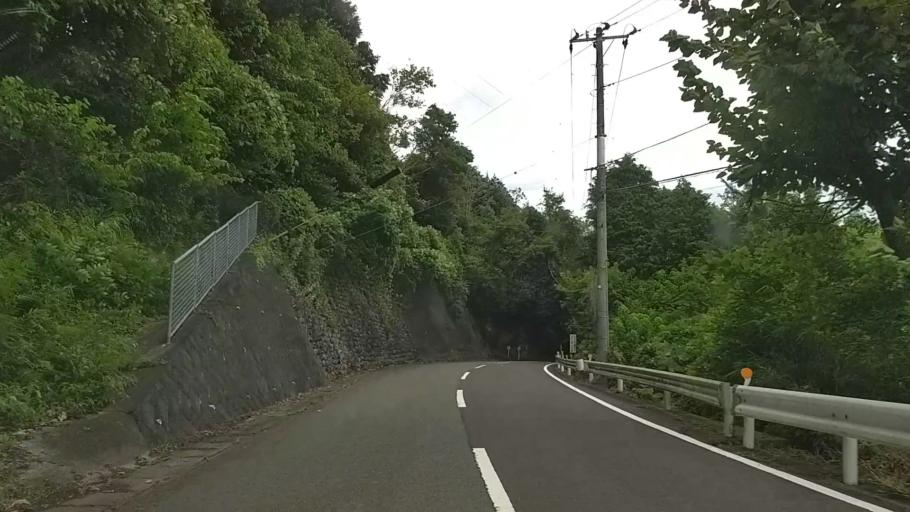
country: JP
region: Yamanashi
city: Uenohara
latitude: 35.5868
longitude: 139.1321
